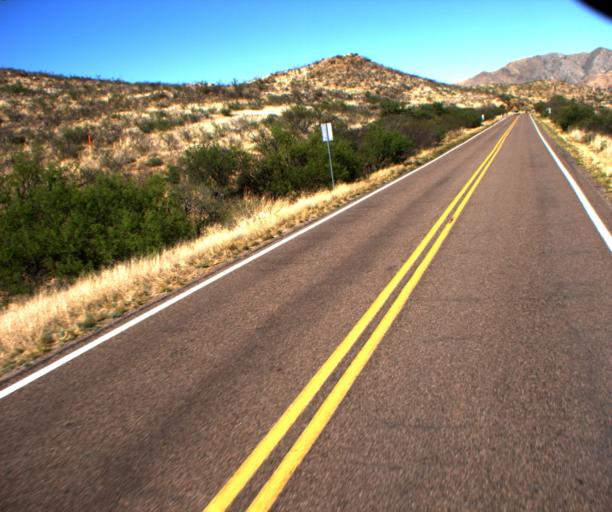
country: US
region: Arizona
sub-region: Pima County
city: Corona de Tucson
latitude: 31.8665
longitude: -110.6870
